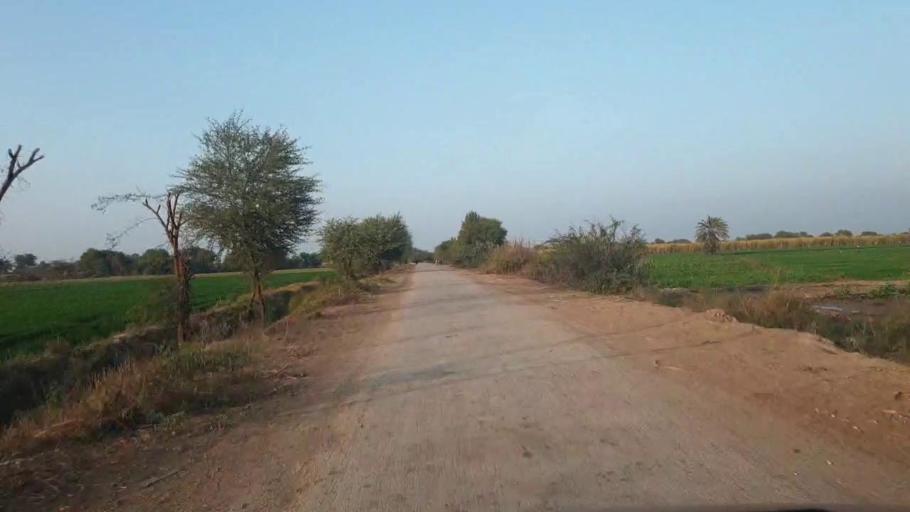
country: PK
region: Sindh
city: Berani
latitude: 25.8345
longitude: 68.7446
